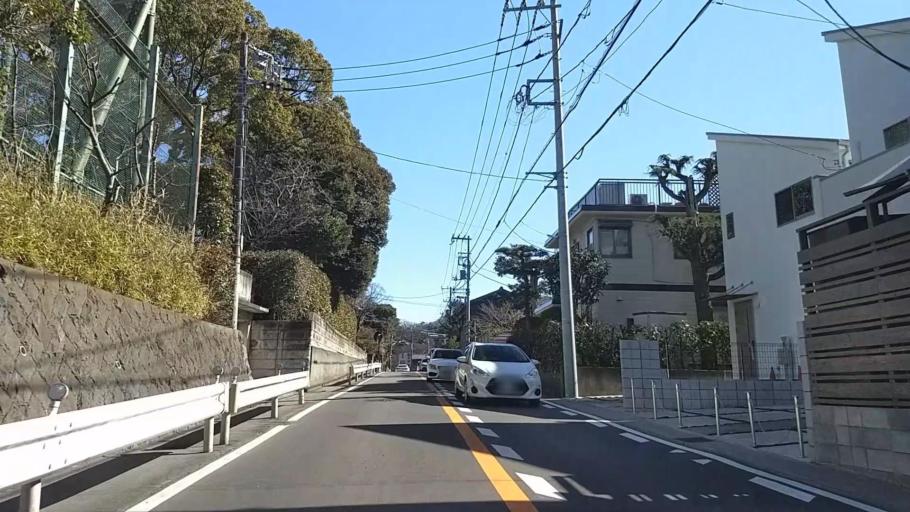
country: JP
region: Kanagawa
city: Kamakura
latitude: 35.3225
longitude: 139.5654
